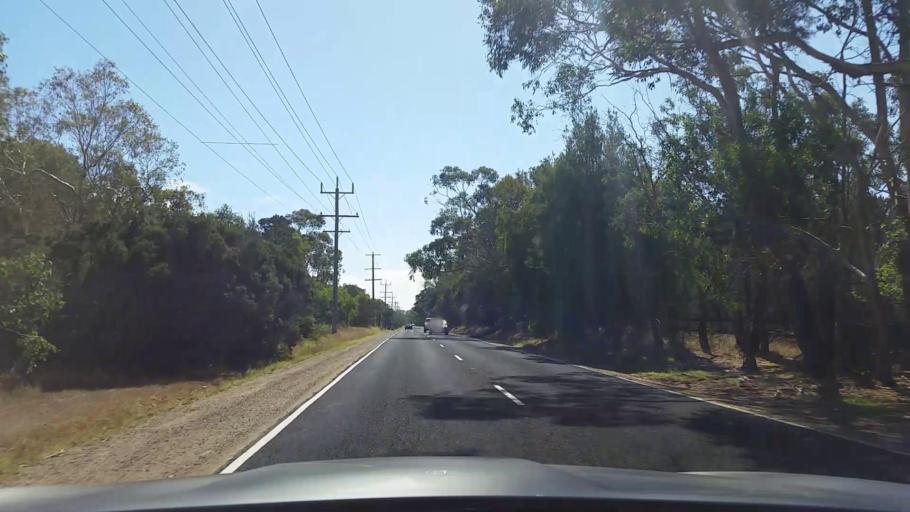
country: AU
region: Victoria
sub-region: Mornington Peninsula
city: Somerville
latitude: -38.2119
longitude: 145.1570
